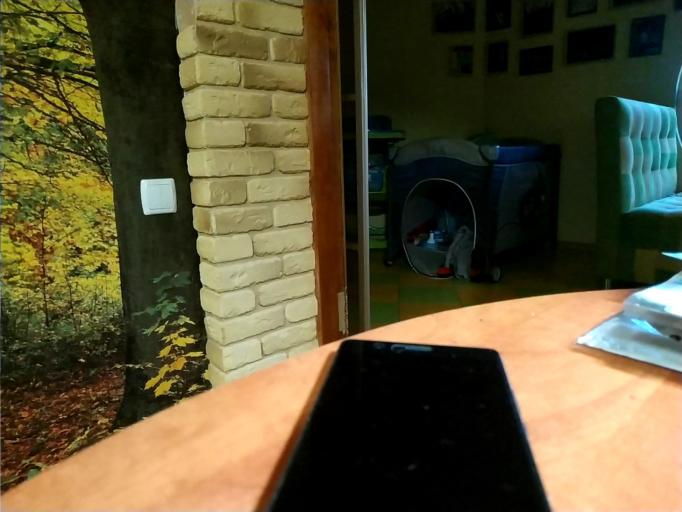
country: RU
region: Orjol
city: Znamenskoye
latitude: 53.4367
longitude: 35.5314
